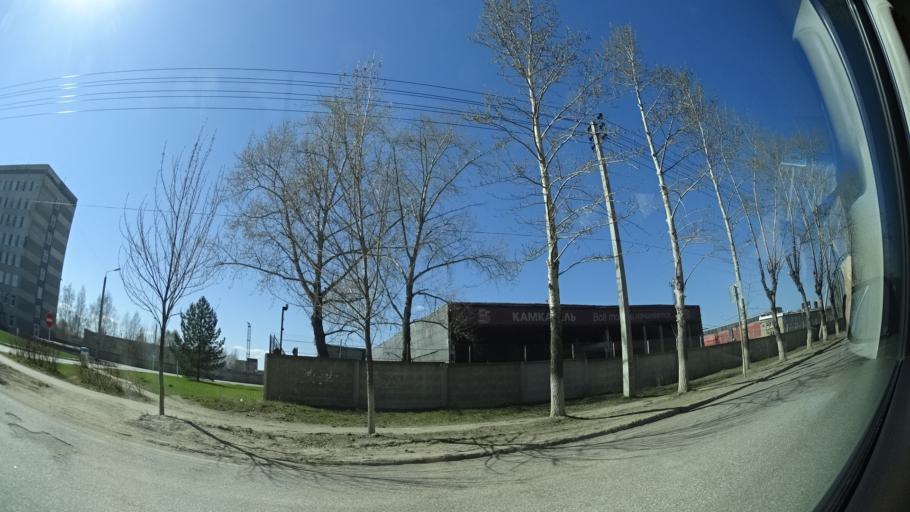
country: RU
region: Perm
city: Perm
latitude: 58.1201
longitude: 56.2929
